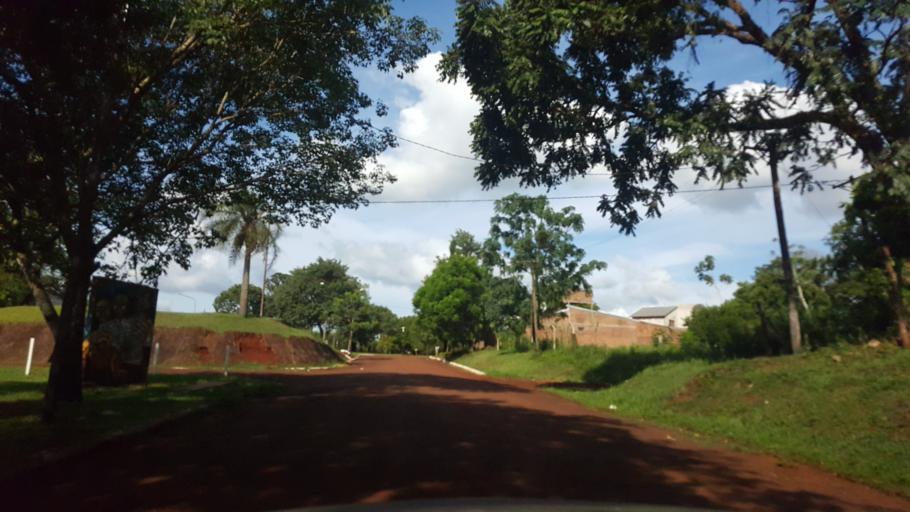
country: AR
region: Misiones
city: Santa Ana
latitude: -27.3702
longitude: -55.5832
